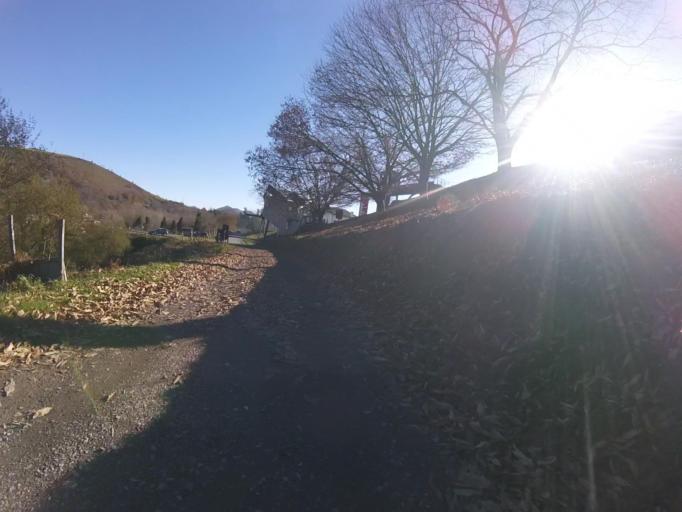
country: ES
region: Navarre
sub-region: Provincia de Navarra
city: Bera
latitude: 43.3102
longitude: -1.6873
